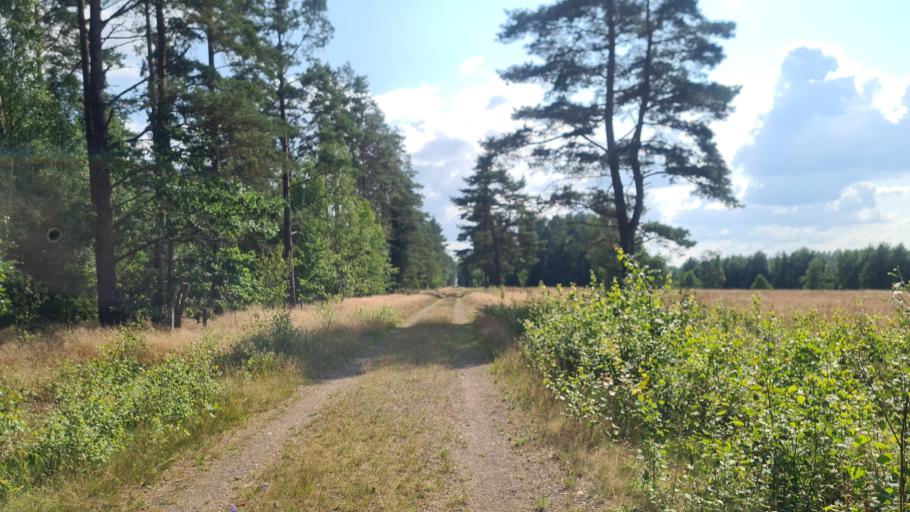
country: SE
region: Kronoberg
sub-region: Ljungby Kommun
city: Ljungby
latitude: 56.7681
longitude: 13.8955
